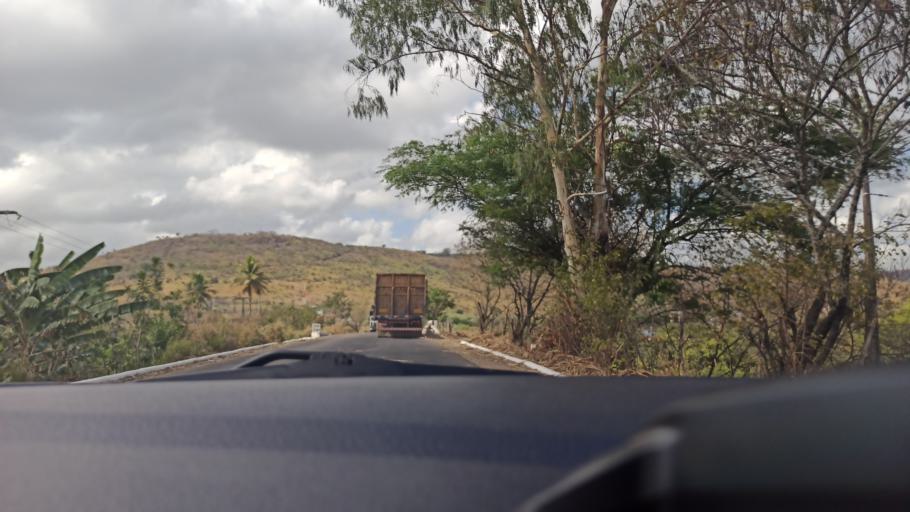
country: BR
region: Pernambuco
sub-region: Timbauba
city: Timbauba
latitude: -7.5170
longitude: -35.3044
